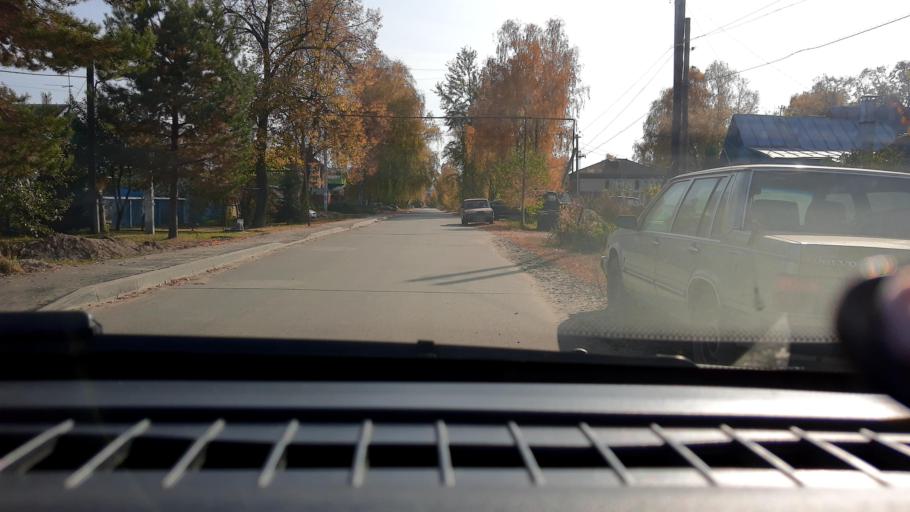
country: RU
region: Nizjnij Novgorod
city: Gorbatovka
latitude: 56.2093
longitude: 43.7586
